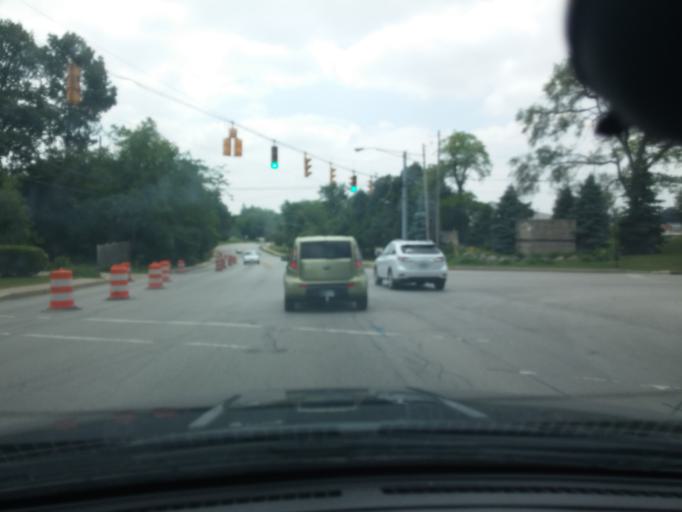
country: US
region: Indiana
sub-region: Tippecanoe County
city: West Lafayette
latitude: 40.4391
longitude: -86.9175
